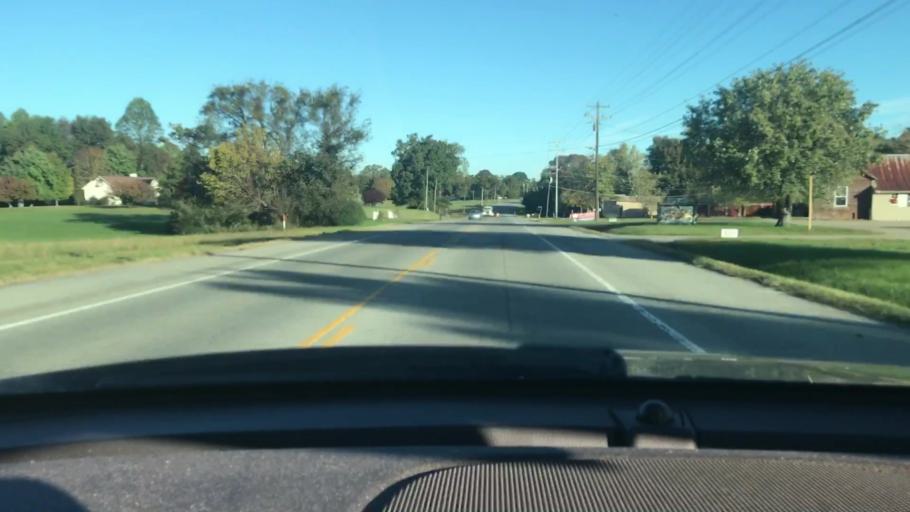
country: US
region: Tennessee
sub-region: Sumner County
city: Millersville
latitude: 36.4146
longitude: -86.6931
